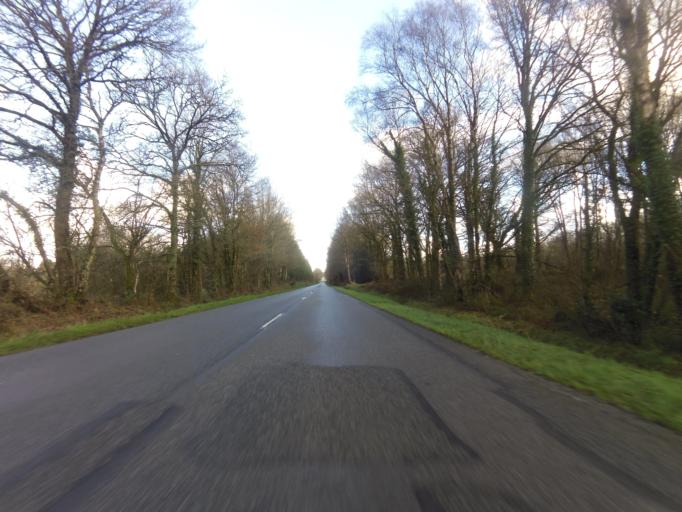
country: FR
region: Brittany
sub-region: Departement du Morbihan
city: Guemene-sur-Scorff
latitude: 48.0672
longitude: -3.1484
